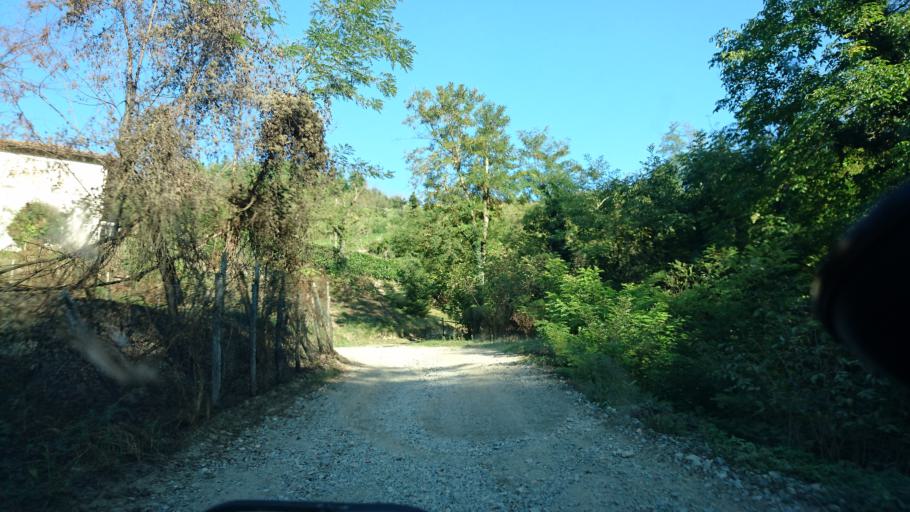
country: IT
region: Piedmont
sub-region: Provincia di Asti
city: Bubbio
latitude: 44.6710
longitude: 8.3041
